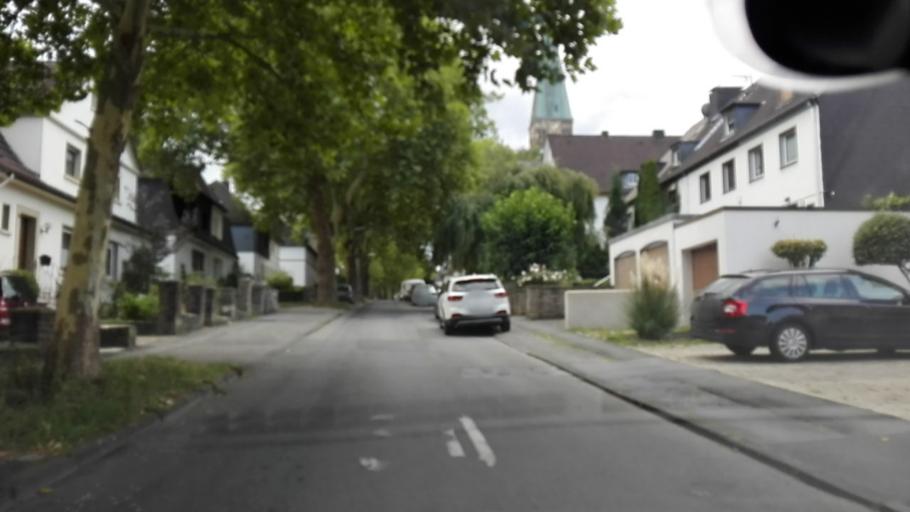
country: DE
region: North Rhine-Westphalia
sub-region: Regierungsbezirk Arnsberg
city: Dortmund
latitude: 51.4848
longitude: 7.4279
